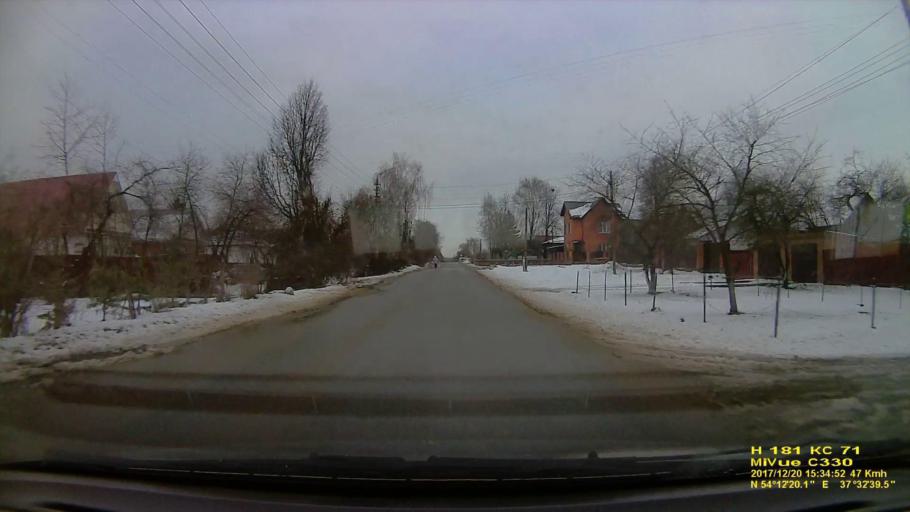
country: RU
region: Tula
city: Tula
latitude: 54.2055
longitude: 37.5444
